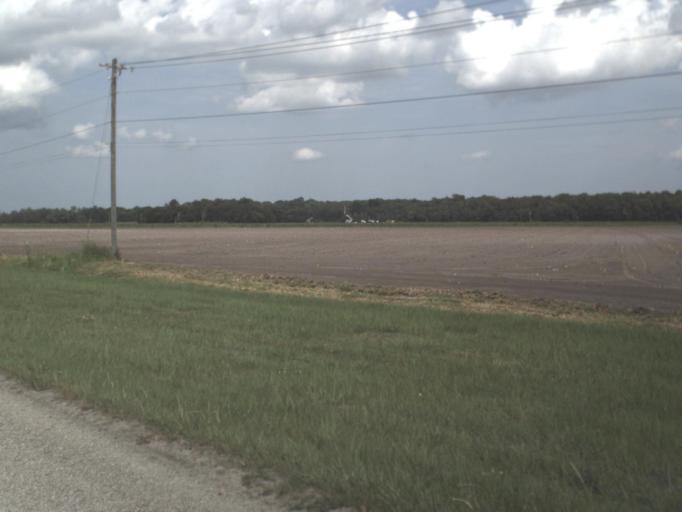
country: US
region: Florida
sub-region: Putnam County
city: East Palatka
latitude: 29.6992
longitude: -81.5542
